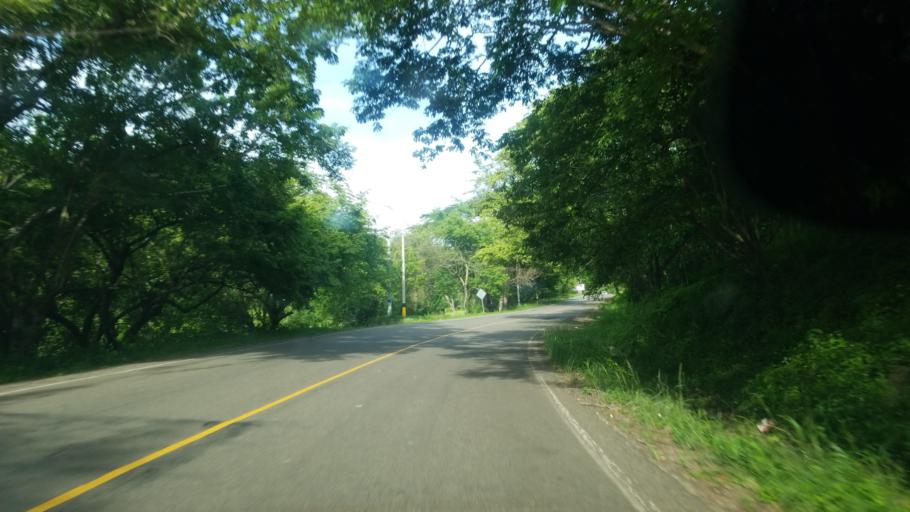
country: HN
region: Santa Barbara
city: Trinidad
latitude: 15.1384
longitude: -88.2302
